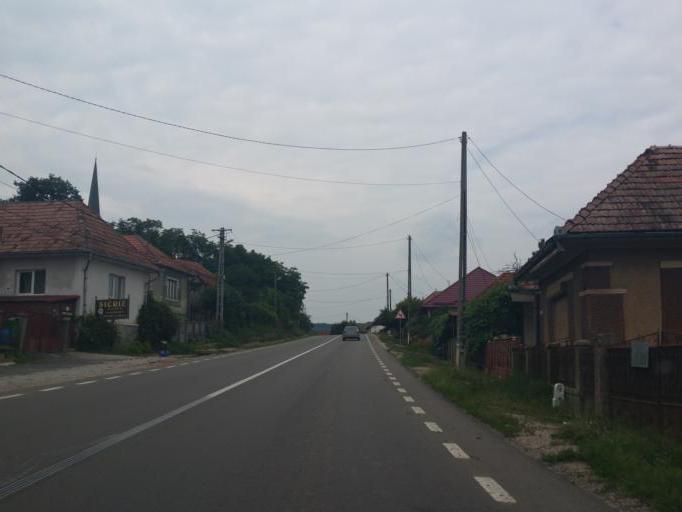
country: RO
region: Salaj
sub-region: Comuna Zimbor
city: Zimbor
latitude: 47.0313
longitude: 23.2700
